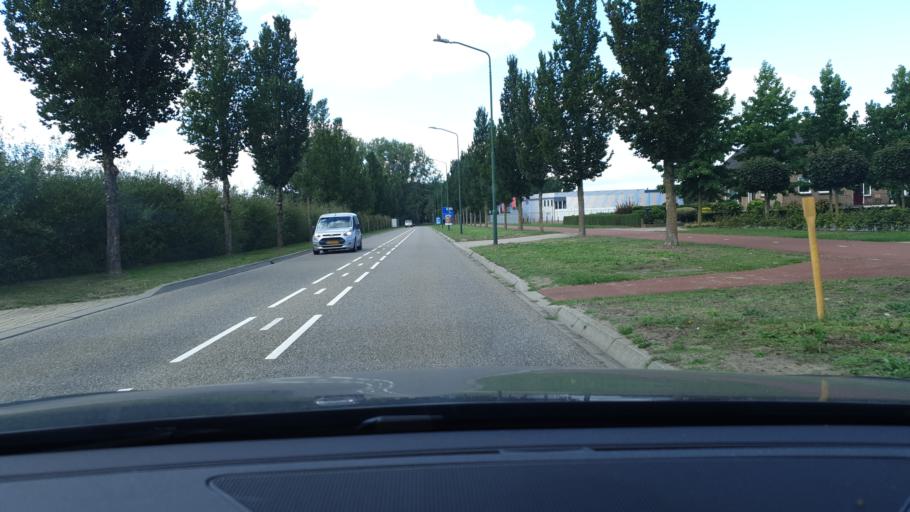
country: NL
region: North Brabant
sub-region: Gemeente Cuijk
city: Cuijk
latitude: 51.7303
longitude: 5.8616
